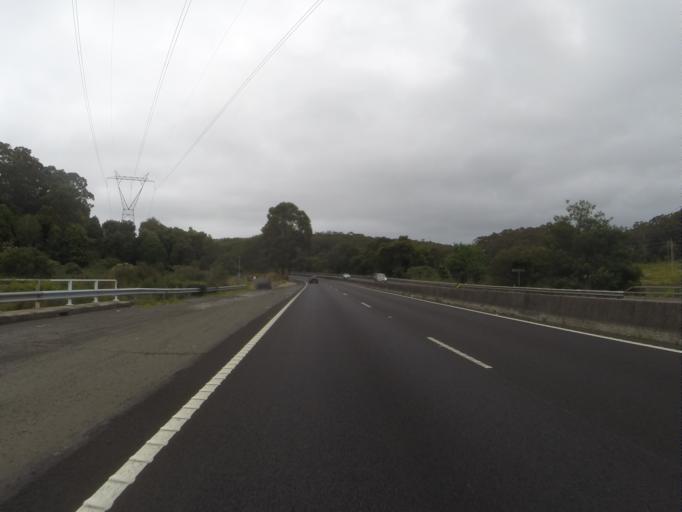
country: AU
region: New South Wales
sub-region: Wollongong
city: Bulli
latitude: -34.3389
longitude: 150.8787
